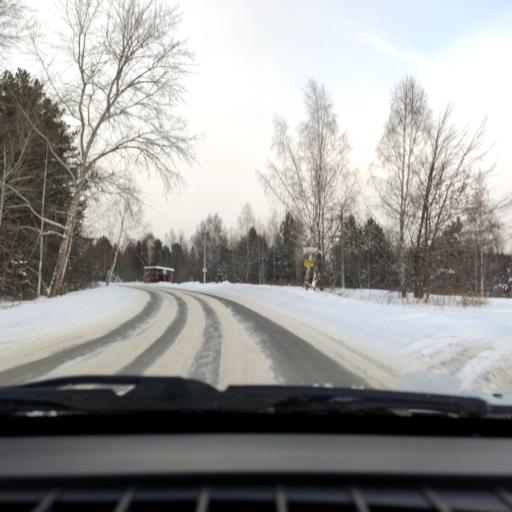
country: RU
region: Perm
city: Overyata
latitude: 58.0474
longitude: 55.8848
